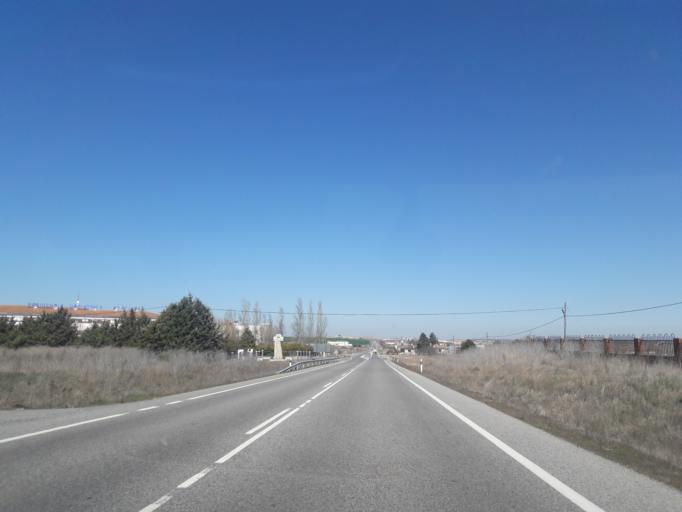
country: ES
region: Castille and Leon
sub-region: Provincia de Salamanca
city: Miranda de Azan
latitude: 40.8926
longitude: -5.6643
